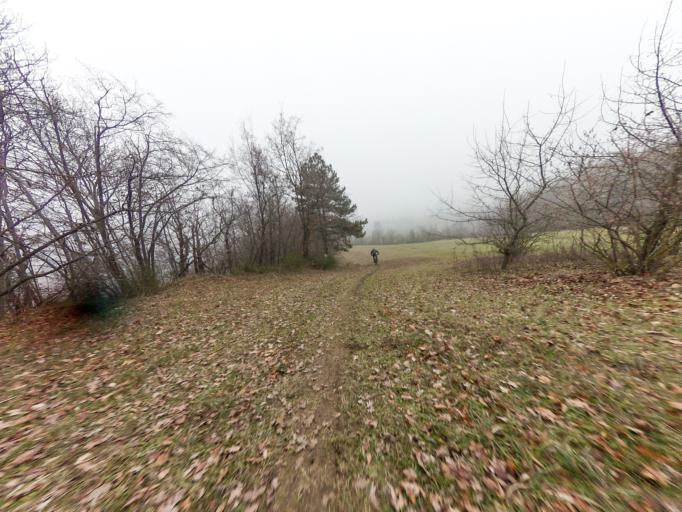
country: IT
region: Emilia-Romagna
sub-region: Provincia di Bologna
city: Pianoro
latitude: 44.3397
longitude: 11.3217
